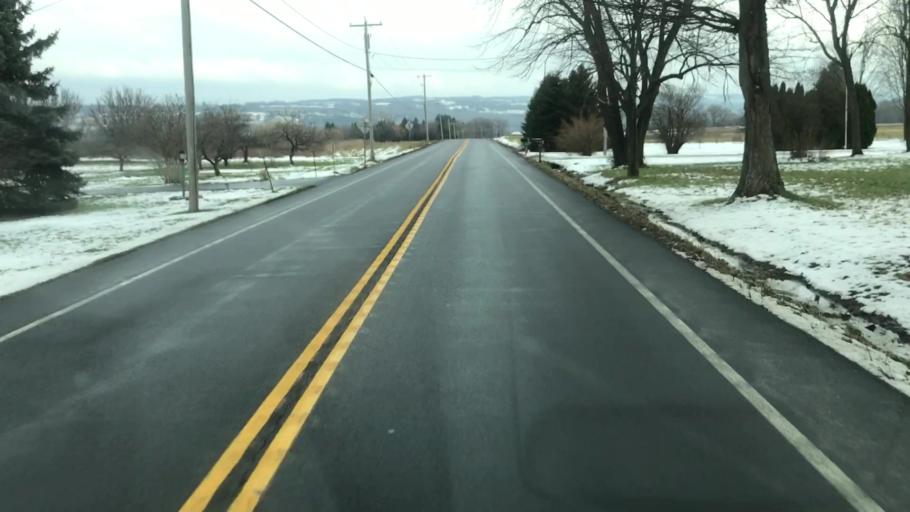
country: US
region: New York
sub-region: Onondaga County
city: Skaneateles
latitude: 42.8389
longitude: -76.3766
